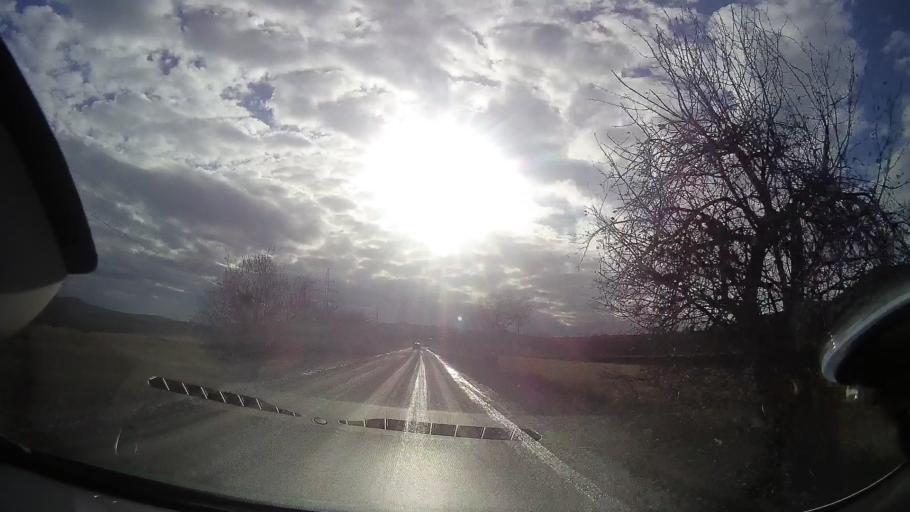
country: RO
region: Cluj
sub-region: Comuna Baisoara
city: Baisoara
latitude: 46.6246
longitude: 23.4535
